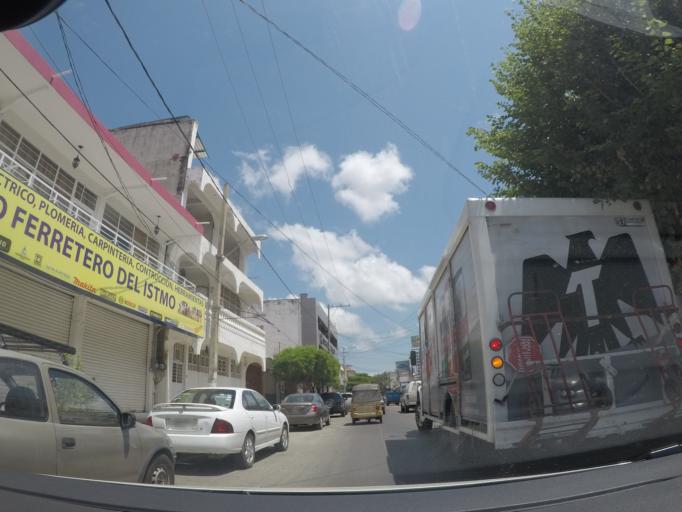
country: MX
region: Oaxaca
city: Juchitan de Zaragoza
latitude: 16.4396
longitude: -95.0222
